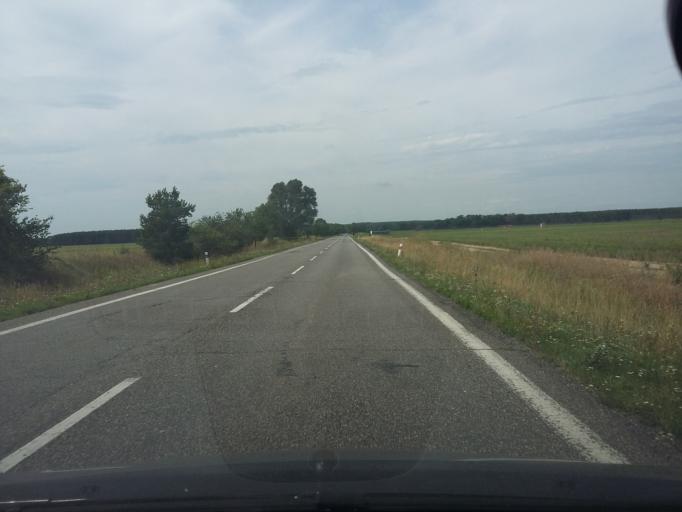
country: SK
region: Bratislavsky
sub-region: Okres Malacky
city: Malacky
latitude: 48.3814
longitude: 17.1159
